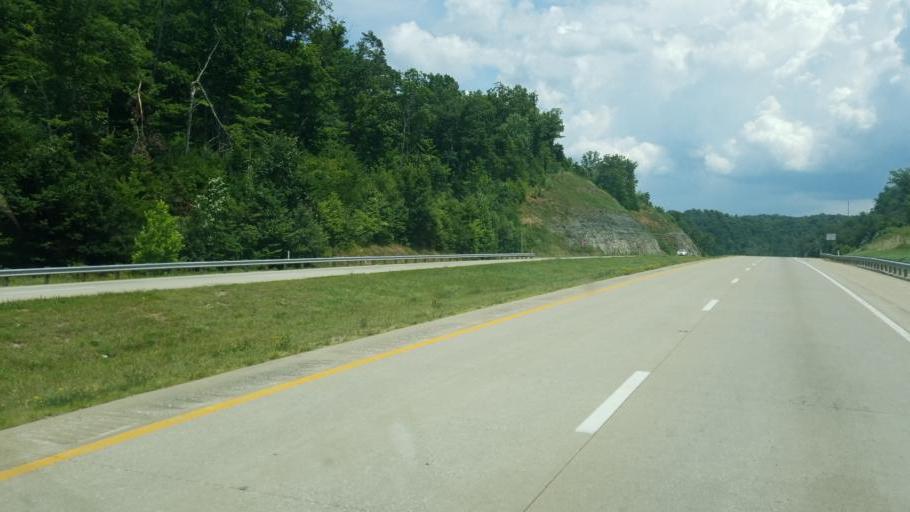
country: US
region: West Virginia
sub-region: Putnam County
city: Eleanor
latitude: 38.5286
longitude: -81.9448
